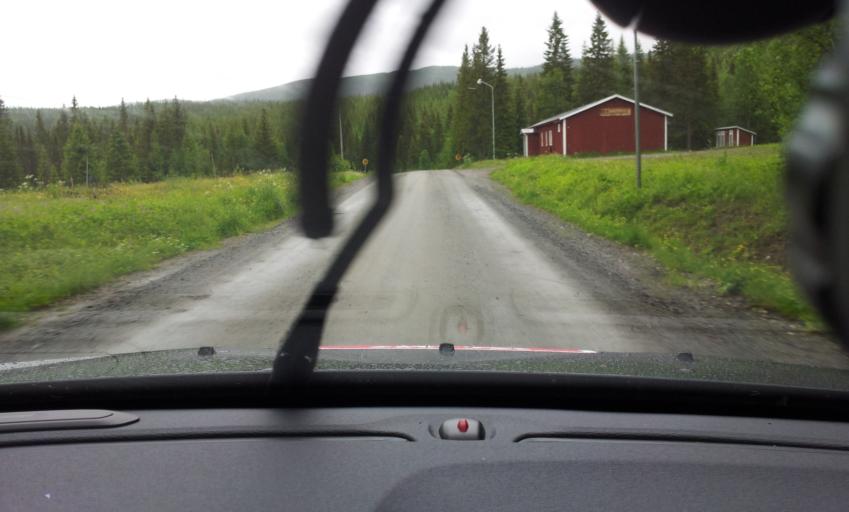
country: SE
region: Jaemtland
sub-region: Are Kommun
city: Are
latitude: 63.4749
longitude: 12.8087
